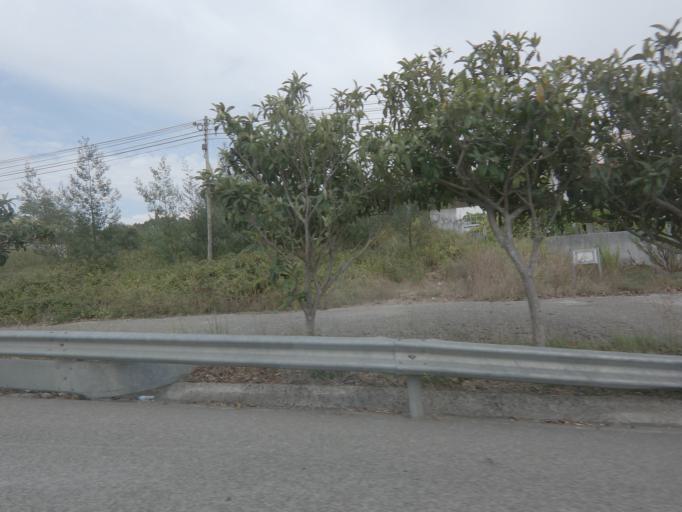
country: PT
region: Coimbra
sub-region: Condeixa-A-Nova
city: Condeixa-a-Nova
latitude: 40.1423
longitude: -8.4661
